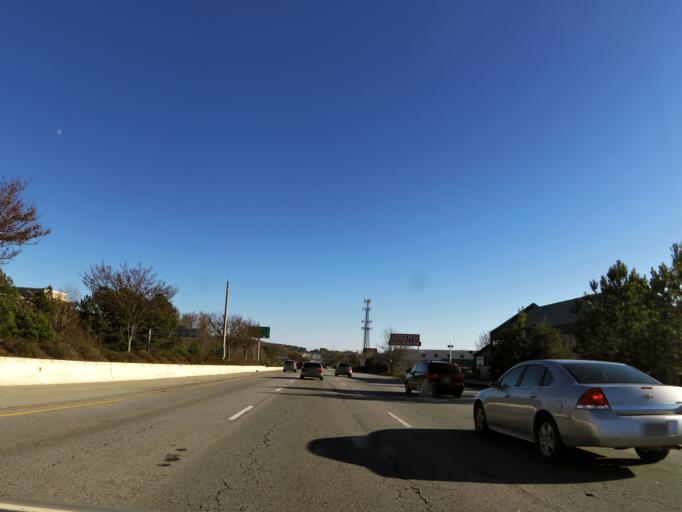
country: US
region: South Carolina
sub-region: Greenville County
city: Wade Hampton
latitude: 34.8521
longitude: -82.3302
